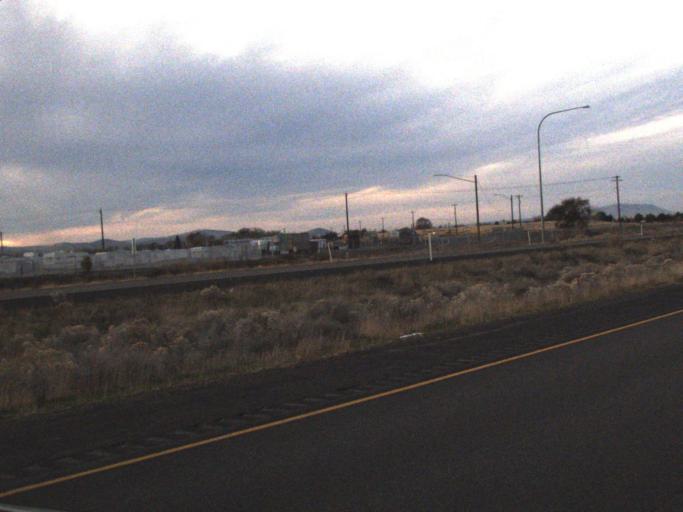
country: US
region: Washington
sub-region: Walla Walla County
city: Burbank
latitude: 46.2329
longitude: -119.0471
